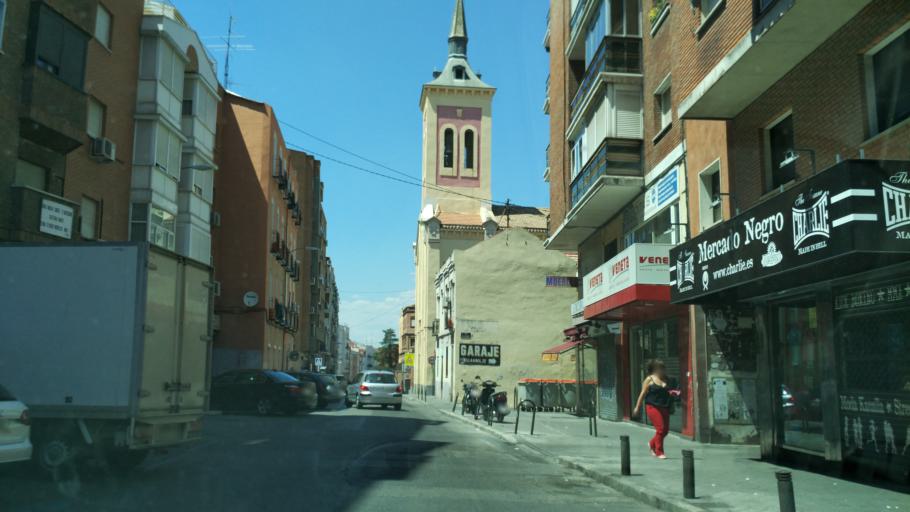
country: ES
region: Madrid
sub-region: Provincia de Madrid
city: Tetuan de las Victorias
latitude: 40.4571
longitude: -3.7053
